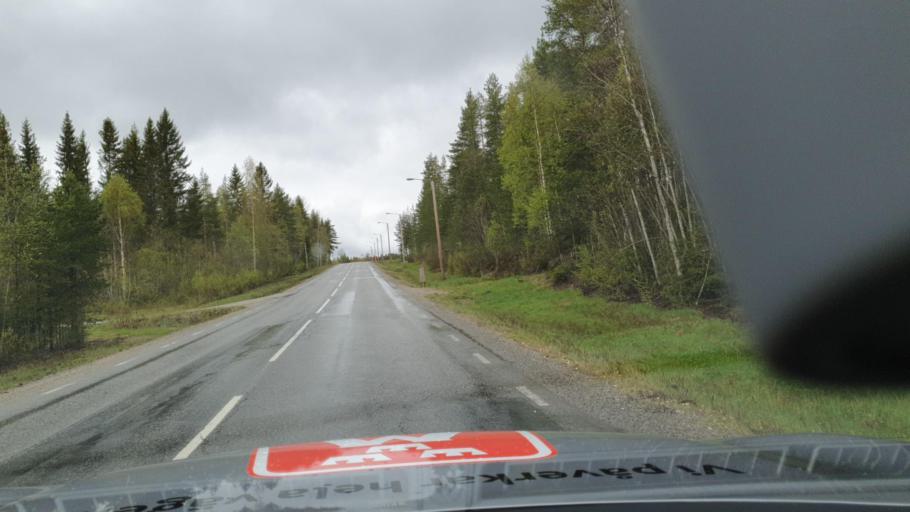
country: SE
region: Vaesternorrland
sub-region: OErnskoeldsviks Kommun
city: Bredbyn
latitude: 63.5066
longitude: 17.8216
